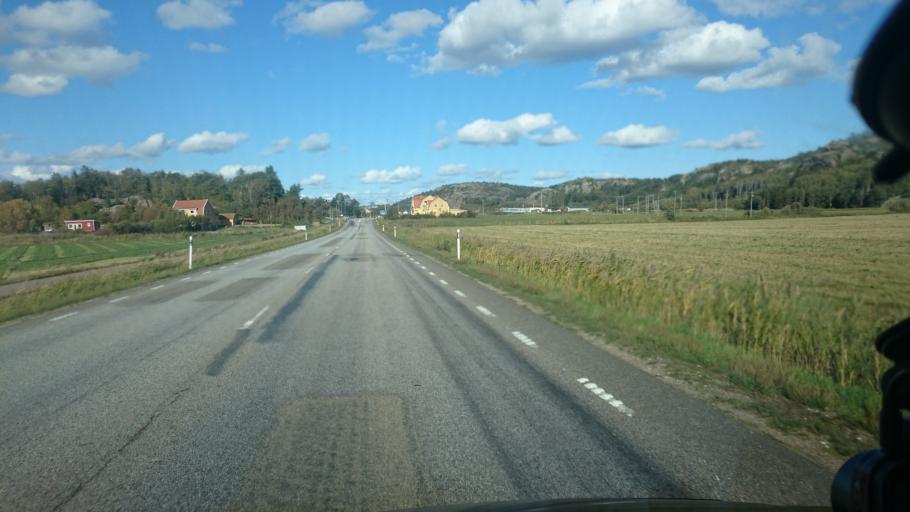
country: SE
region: Vaestra Goetaland
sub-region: Lysekils Kommun
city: Lysekil
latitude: 58.3146
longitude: 11.4839
